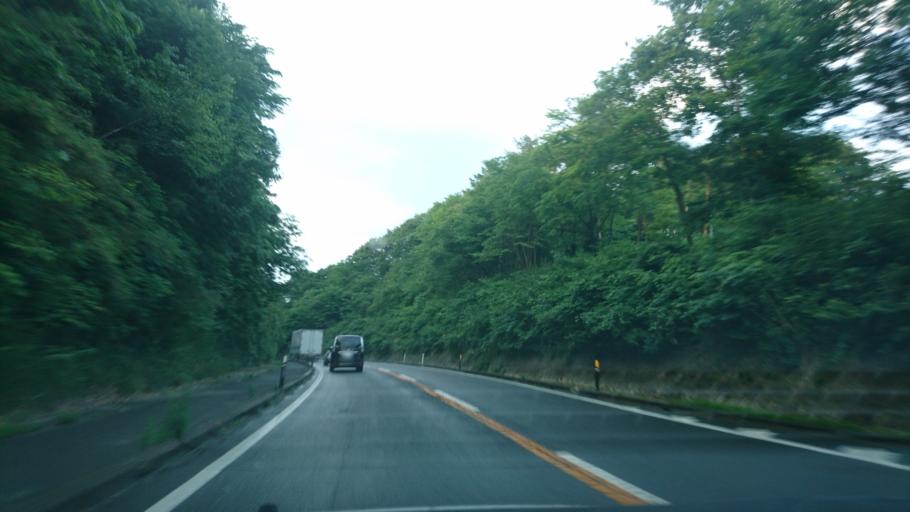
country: JP
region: Iwate
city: Ichinoseki
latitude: 38.9467
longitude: 141.1175
